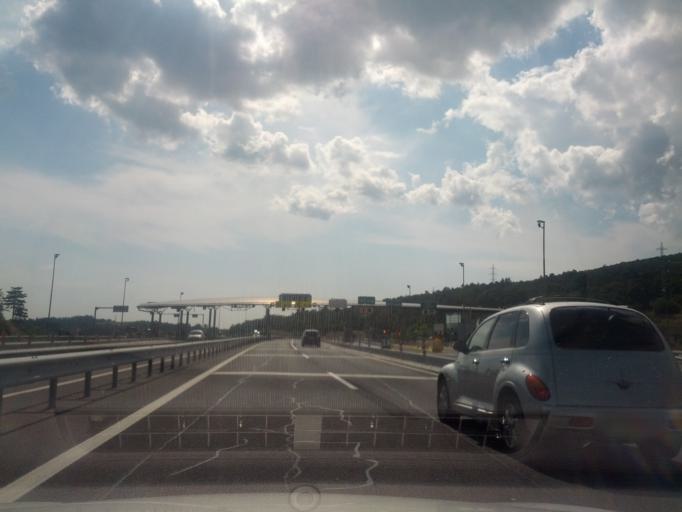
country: SI
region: Hrpelje-Kozina
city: Kozina
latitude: 45.6136
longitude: 13.9402
